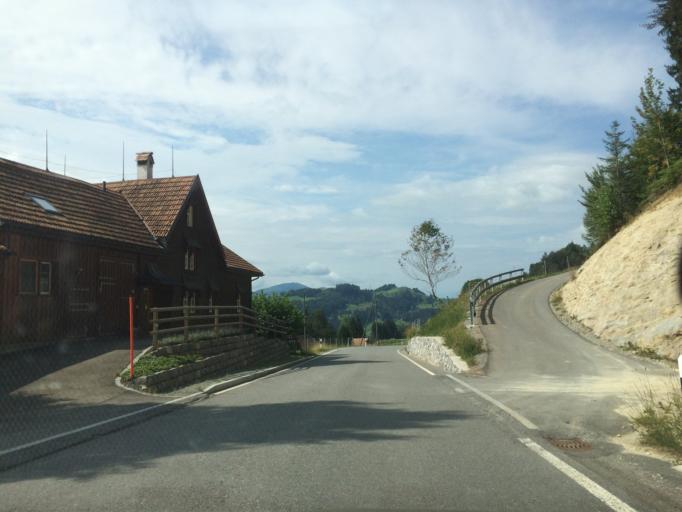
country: CH
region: Appenzell Ausserrhoden
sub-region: Bezirk Mittelland
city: Buhler
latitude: 47.3842
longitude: 9.4452
